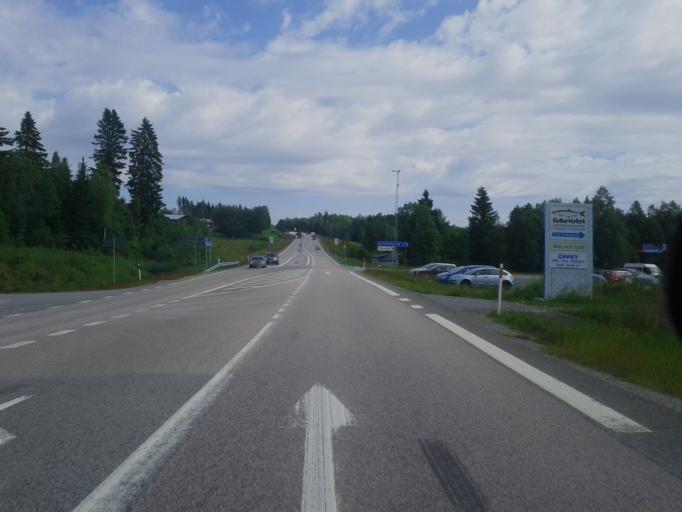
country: SE
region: Vaesternorrland
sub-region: OErnskoeldsviks Kommun
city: Ornskoldsvik
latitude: 63.2962
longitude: 18.8854
